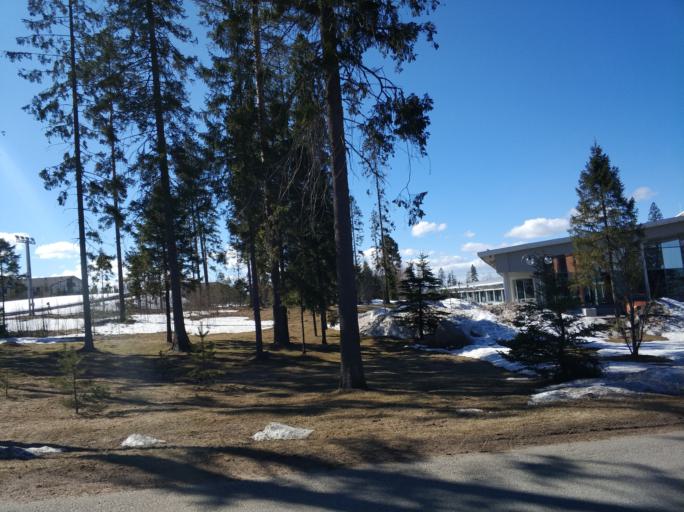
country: RU
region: Leningrad
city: Sosnovo
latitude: 60.5164
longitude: 30.2100
